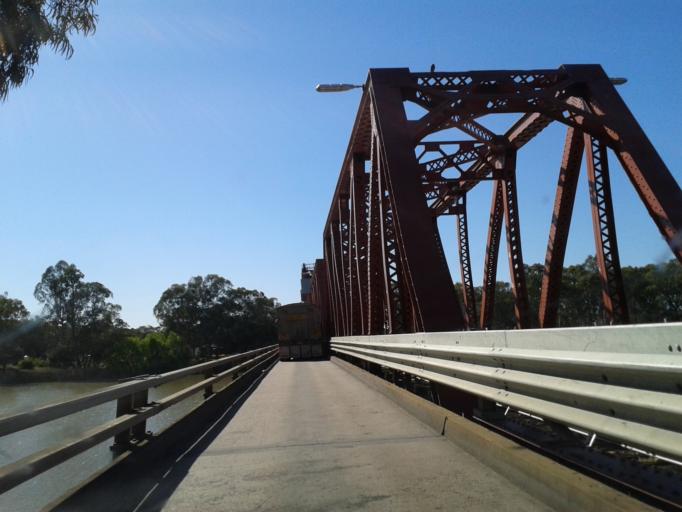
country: AU
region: South Australia
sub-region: Renmark Paringa
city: Renmark
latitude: -34.1807
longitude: 140.7754
